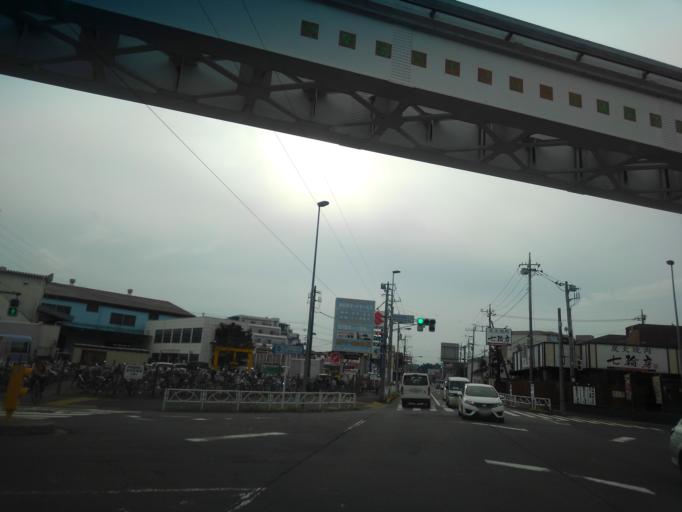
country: JP
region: Tokyo
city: Hino
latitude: 35.6790
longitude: 139.4083
